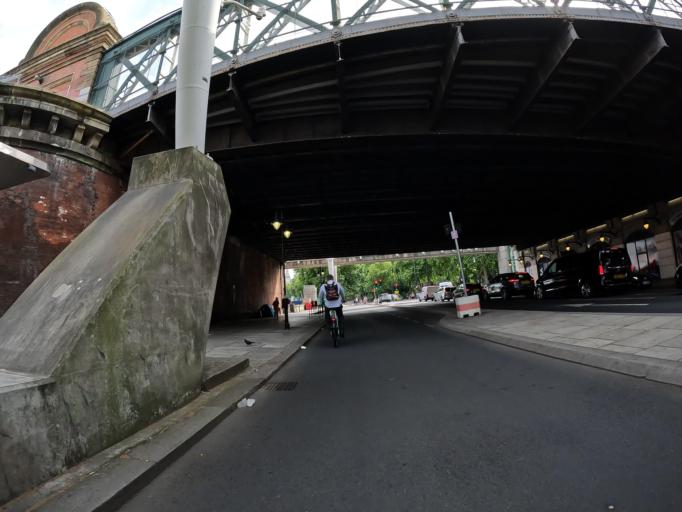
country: GB
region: England
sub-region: Greater London
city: Catford
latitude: 51.4655
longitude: -0.0231
